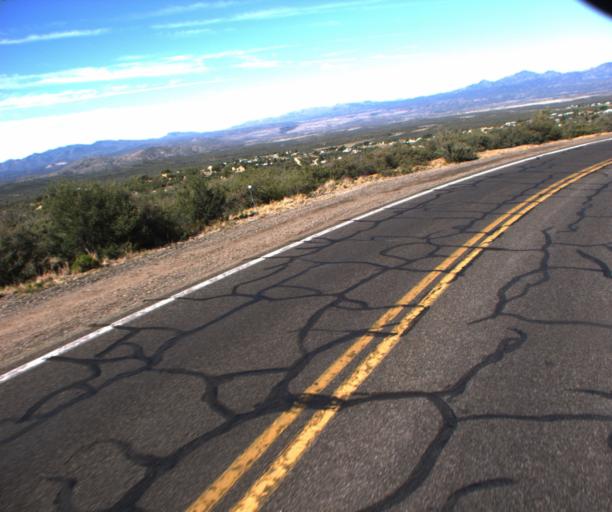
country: US
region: Arizona
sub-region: Yavapai County
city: Prescott
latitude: 34.4234
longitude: -112.5778
